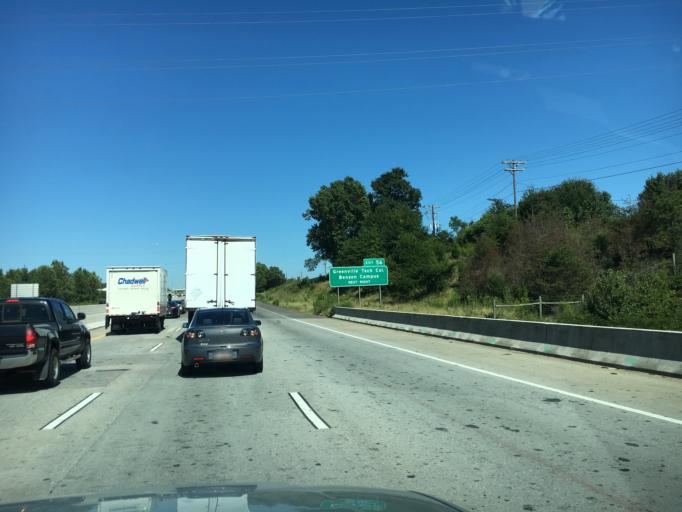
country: US
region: South Carolina
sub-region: Greenville County
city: Five Forks
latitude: 34.8677
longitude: -82.2353
